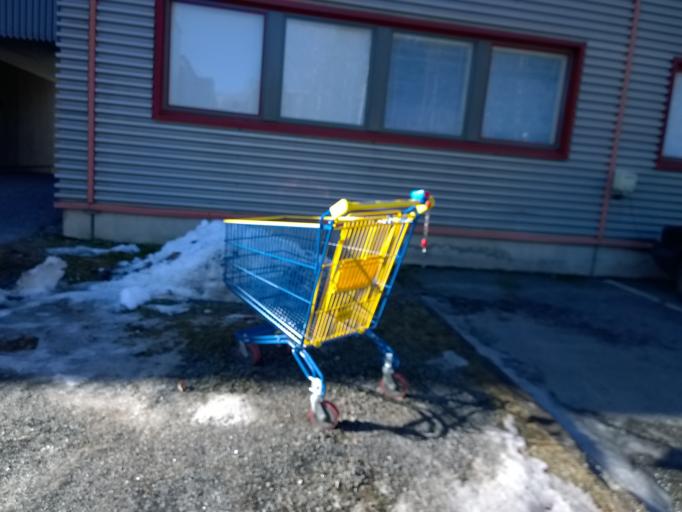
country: FI
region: Pirkanmaa
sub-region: Tampere
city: Tampere
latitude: 61.4509
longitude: 23.8587
